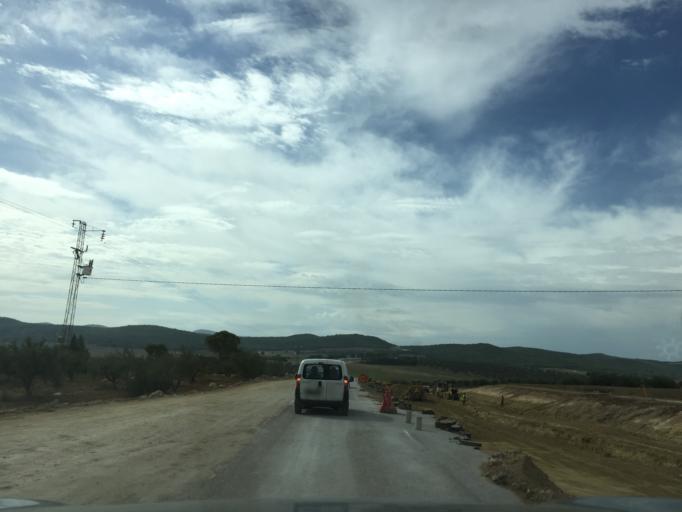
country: TN
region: Zaghwan
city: El Fahs
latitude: 36.2885
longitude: 9.8076
